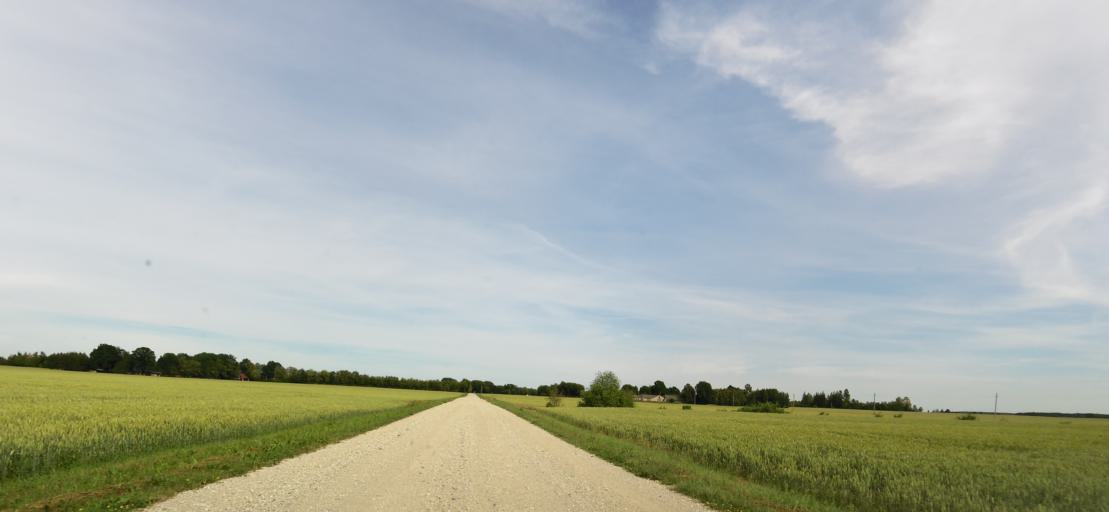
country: LT
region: Panevezys
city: Pasvalys
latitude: 55.9656
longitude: 24.3243
